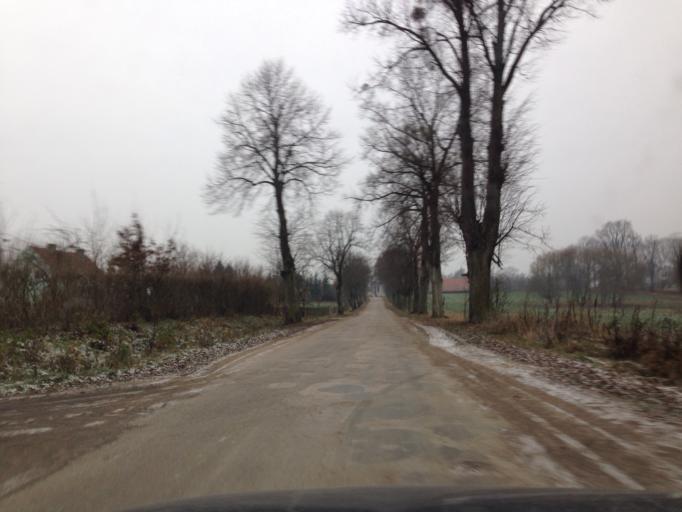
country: RU
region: Kaliningrad
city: Zheleznodorozhnyy
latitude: 54.3124
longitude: 21.2598
